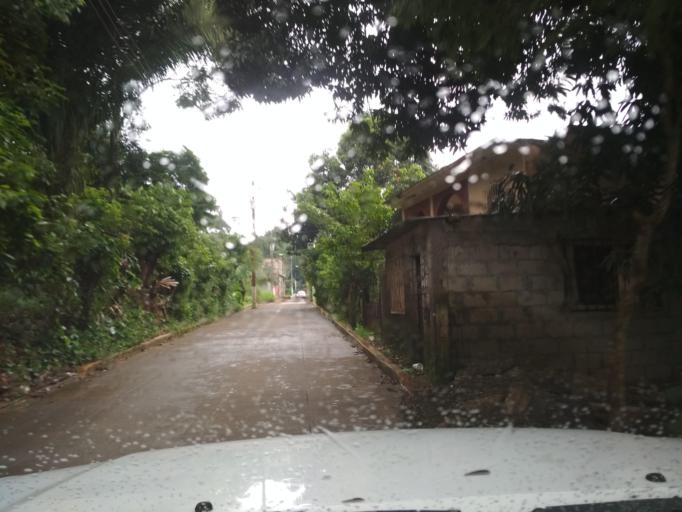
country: MX
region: Veracruz
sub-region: San Andres Tuxtla
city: Tonalapan
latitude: 18.4560
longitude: -95.2263
